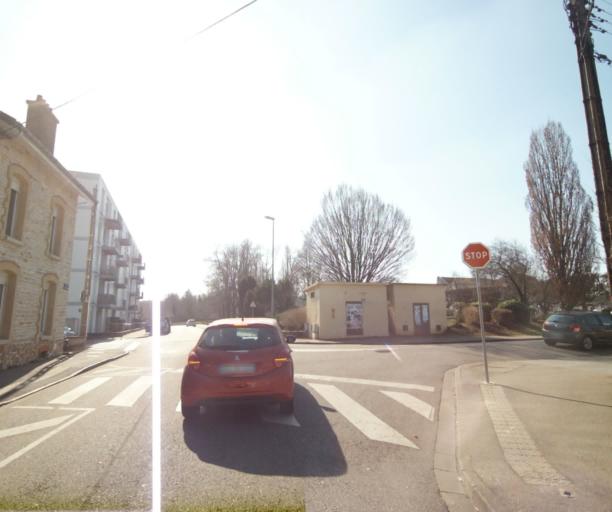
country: FR
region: Lorraine
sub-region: Departement de Meurthe-et-Moselle
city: Jarville-la-Malgrange
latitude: 48.6659
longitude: 6.1985
